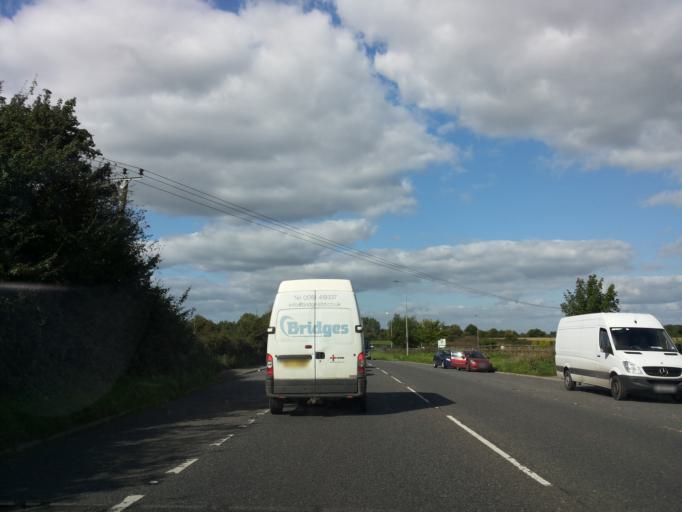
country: GB
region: England
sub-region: Wiltshire
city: Chapmanslade
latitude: 51.2613
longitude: -2.2750
